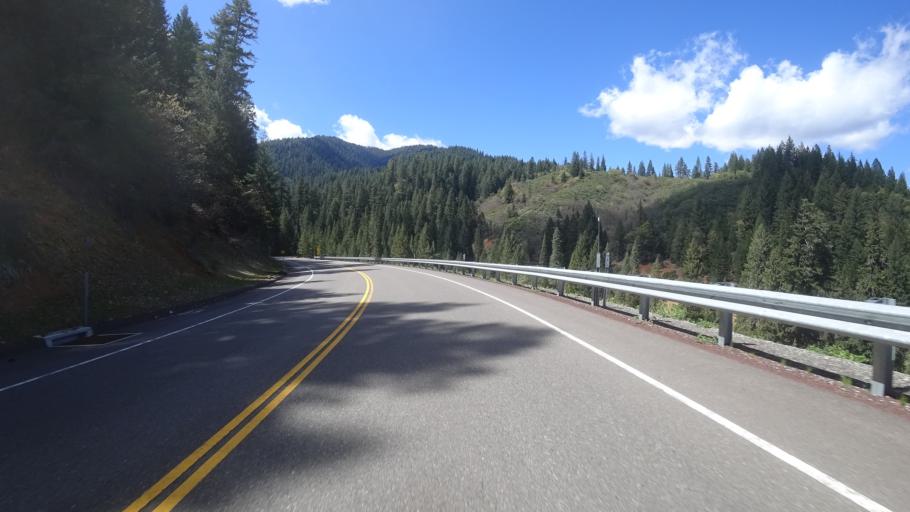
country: US
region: California
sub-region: Trinity County
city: Weaverville
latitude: 40.8267
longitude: -122.8880
